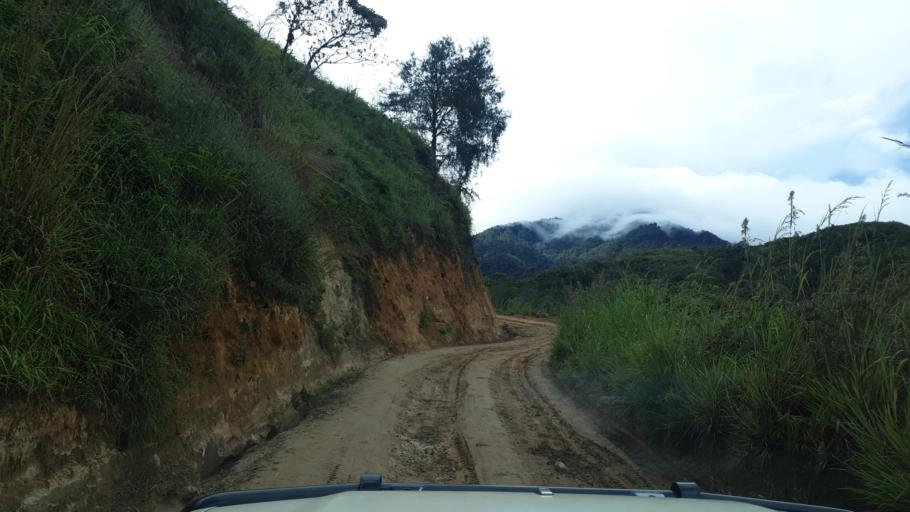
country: PG
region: Eastern Highlands
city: Goroka
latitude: -5.9248
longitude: 145.2633
